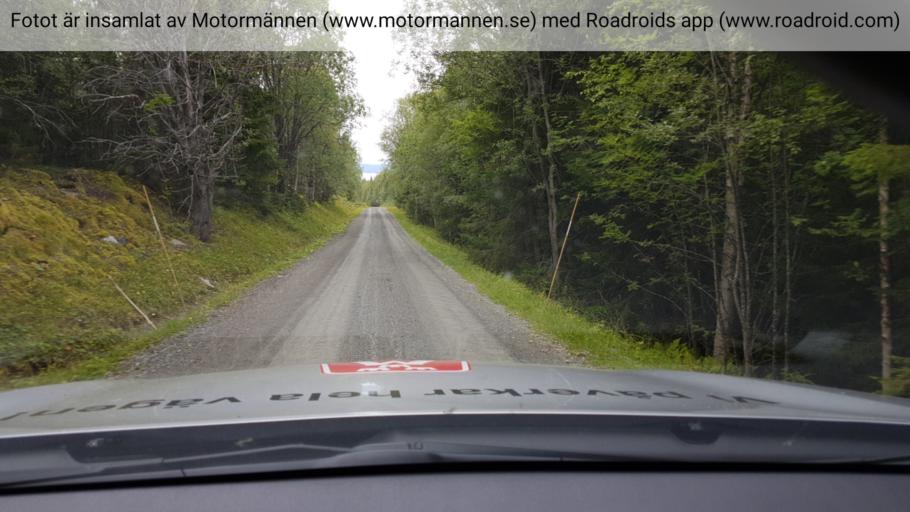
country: SE
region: Jaemtland
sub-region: Krokoms Kommun
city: Valla
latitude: 63.5919
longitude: 14.0008
